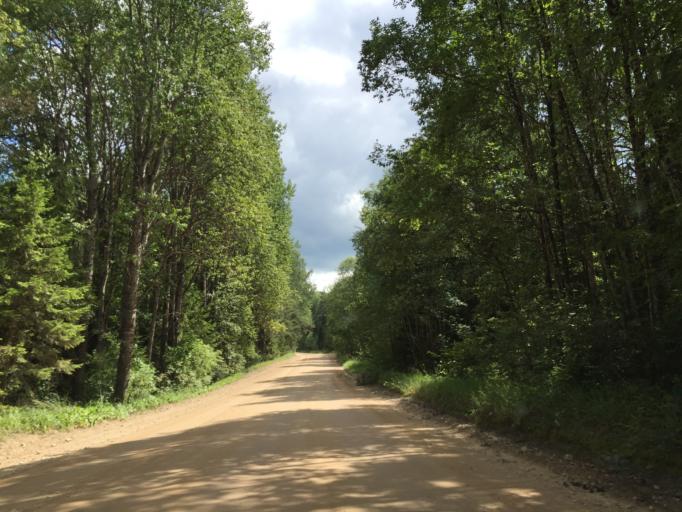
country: LV
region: Ropazu
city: Ropazi
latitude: 56.9168
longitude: 24.7444
